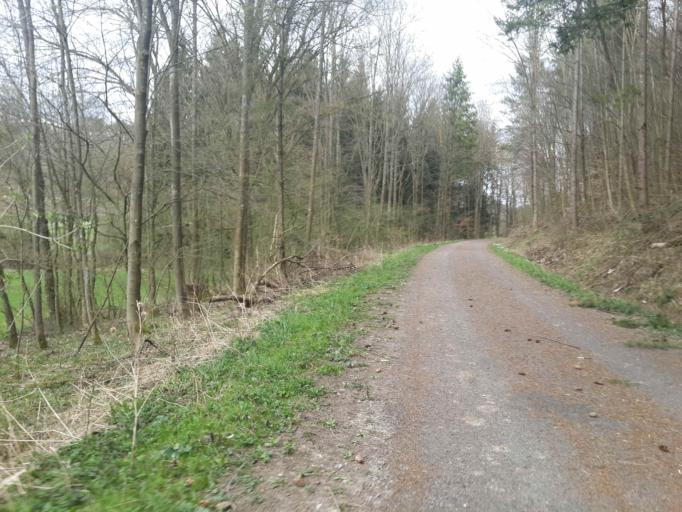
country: DE
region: Baden-Wuerttemberg
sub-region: Karlsruhe Region
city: Billigheim
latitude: 49.3368
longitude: 9.2477
